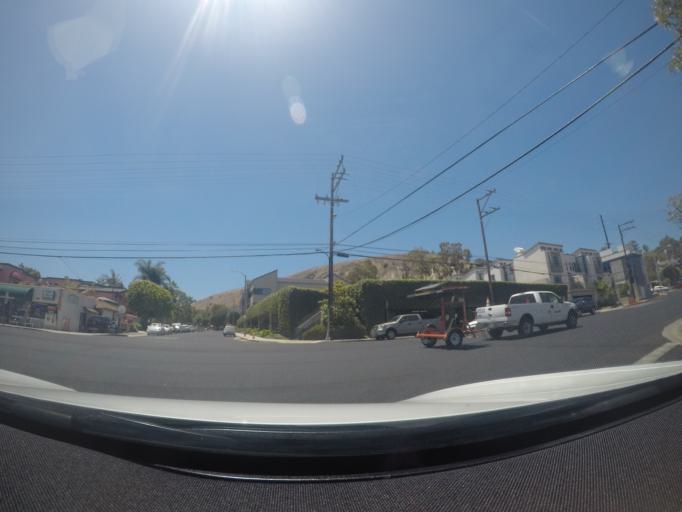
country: US
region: California
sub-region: Los Angeles County
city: Rolling Hills Estates
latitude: 33.7995
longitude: -118.3500
